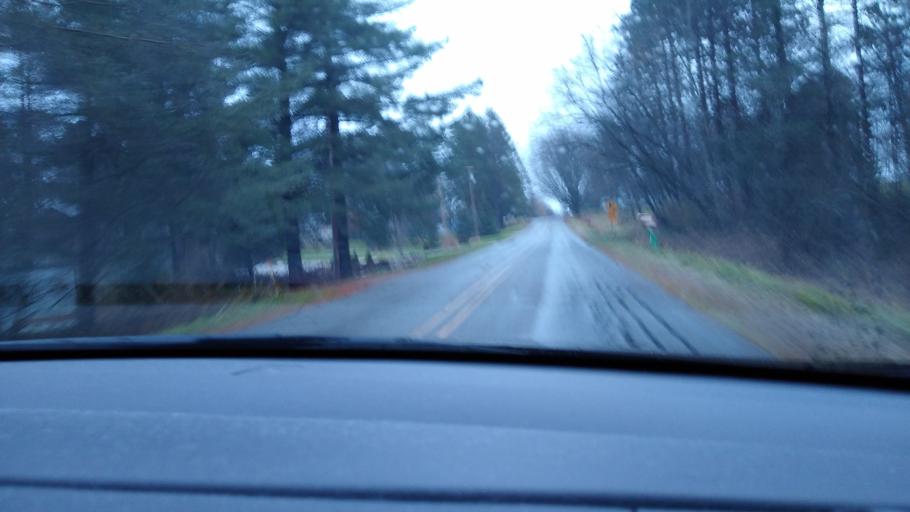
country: US
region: Michigan
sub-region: Wexford County
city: Cadillac
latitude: 44.1821
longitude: -85.3954
